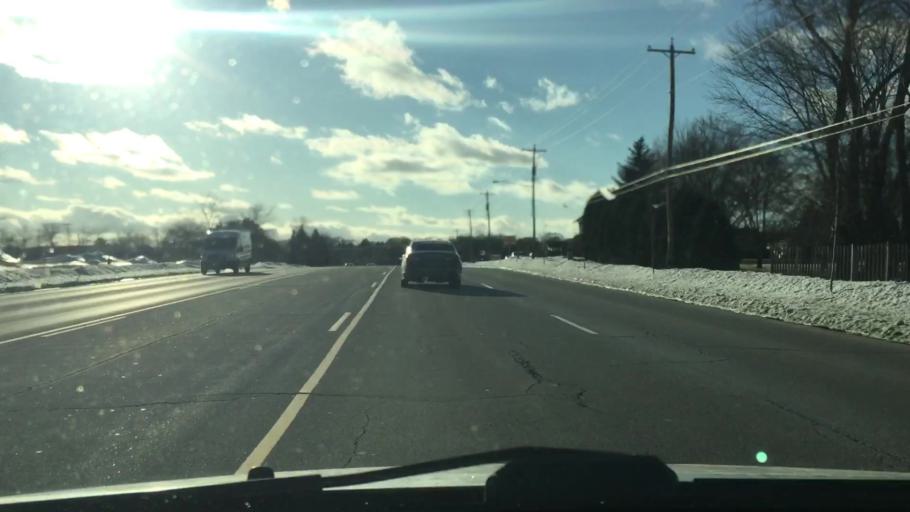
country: US
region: Wisconsin
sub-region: Waukesha County
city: New Berlin
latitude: 42.9841
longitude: -88.0947
